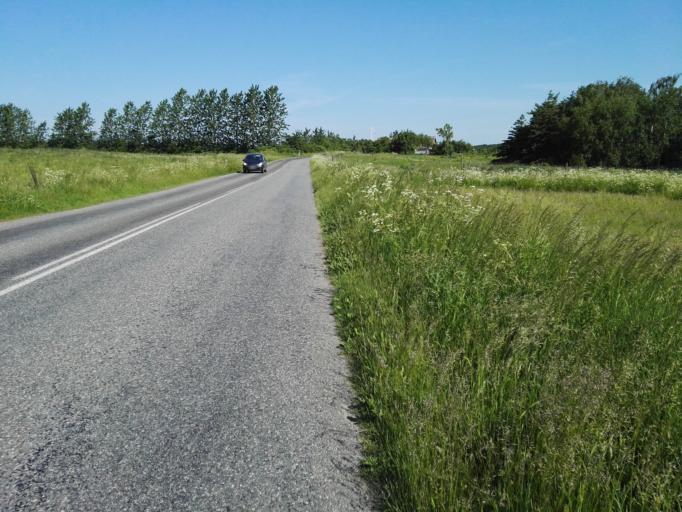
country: DK
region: Zealand
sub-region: Lejre Kommune
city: Ejby
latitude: 55.7209
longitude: 11.8892
